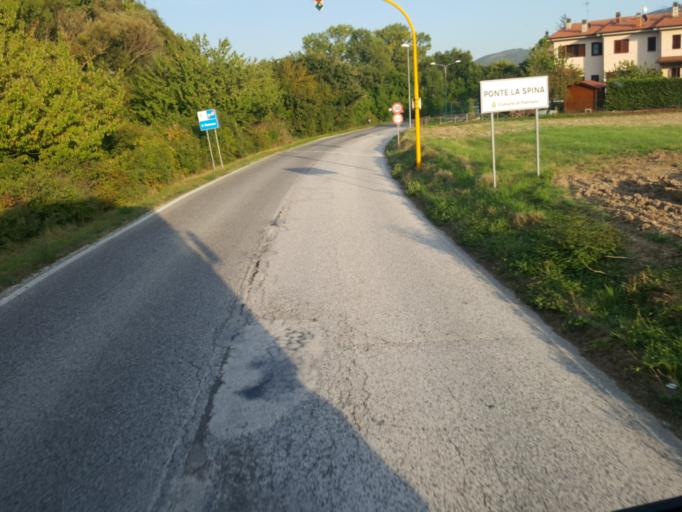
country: IT
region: The Marches
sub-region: Provincia di Ancona
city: Fabriano
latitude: 43.3498
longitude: 12.8352
